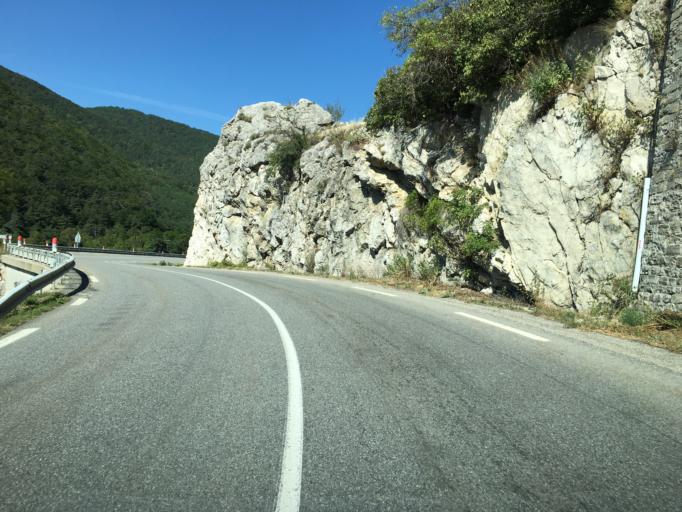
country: FR
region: Provence-Alpes-Cote d'Azur
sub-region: Departement des Hautes-Alpes
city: Veynes
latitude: 44.5883
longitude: 5.7211
